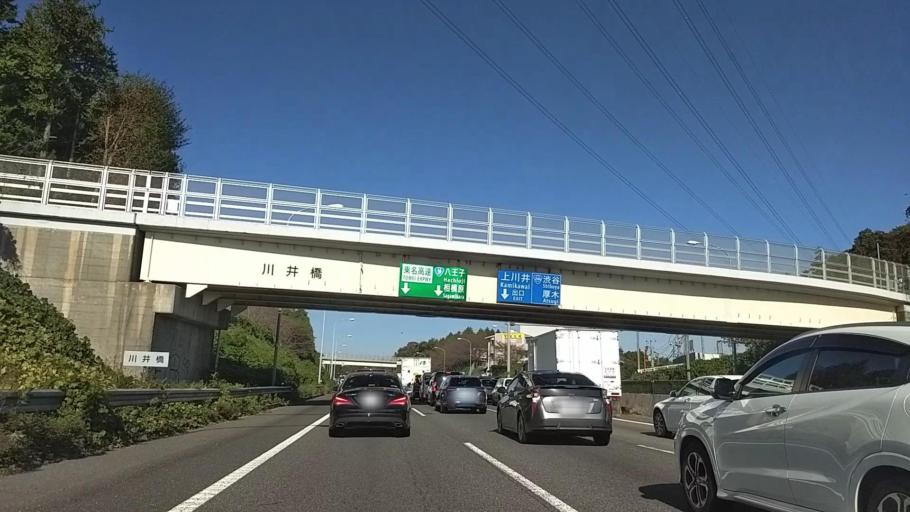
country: JP
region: Kanagawa
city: Minami-rinkan
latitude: 35.4897
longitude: 139.5057
